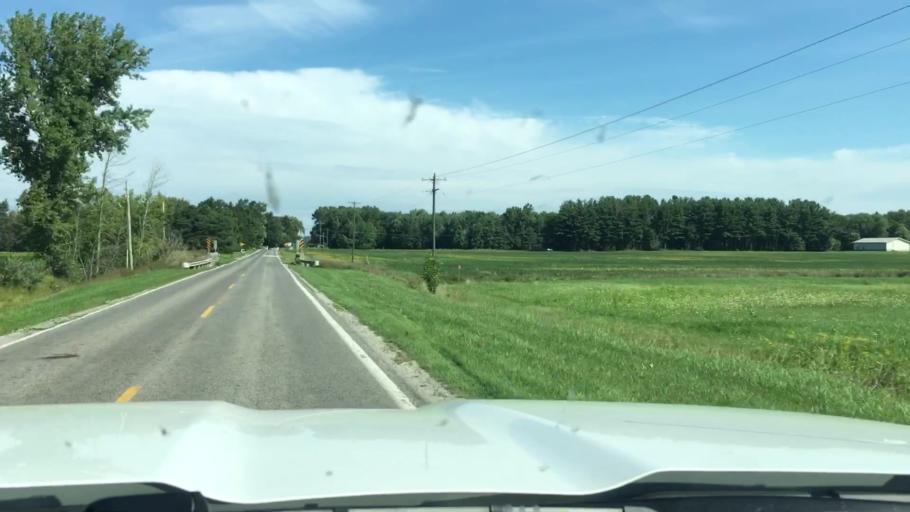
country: US
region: Michigan
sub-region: Saginaw County
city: Hemlock
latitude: 43.4775
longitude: -84.2303
